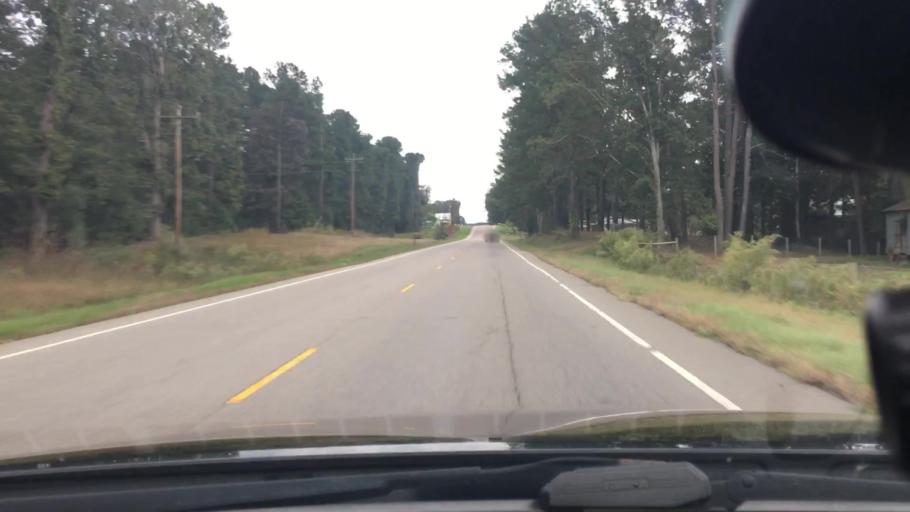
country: US
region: North Carolina
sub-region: Moore County
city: Carthage
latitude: 35.3872
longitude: -79.5009
